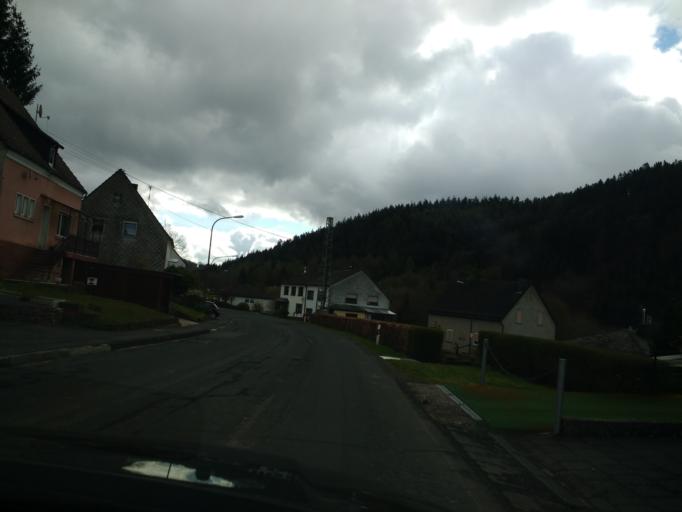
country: DE
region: Rheinland-Pfalz
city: Kalenborn-Scheuern
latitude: 50.2417
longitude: 6.5986
